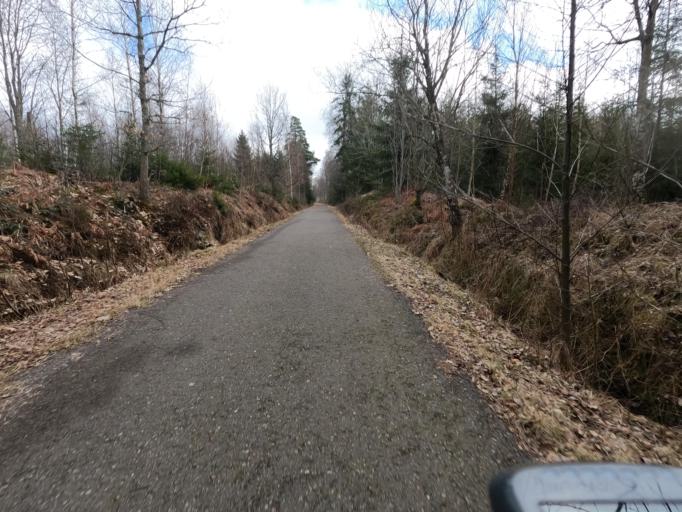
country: SE
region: Joenkoeping
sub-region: Varnamo Kommun
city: Rydaholm
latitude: 56.8553
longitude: 14.1854
